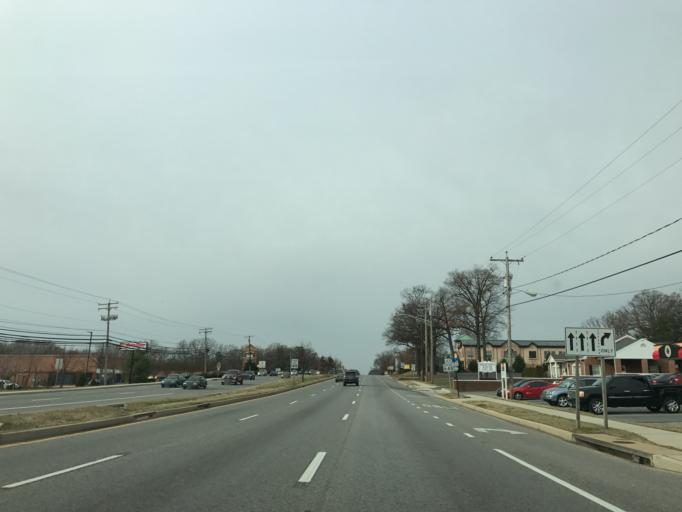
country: US
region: Maryland
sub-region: Anne Arundel County
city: Severna Park
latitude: 39.0811
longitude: -76.5490
